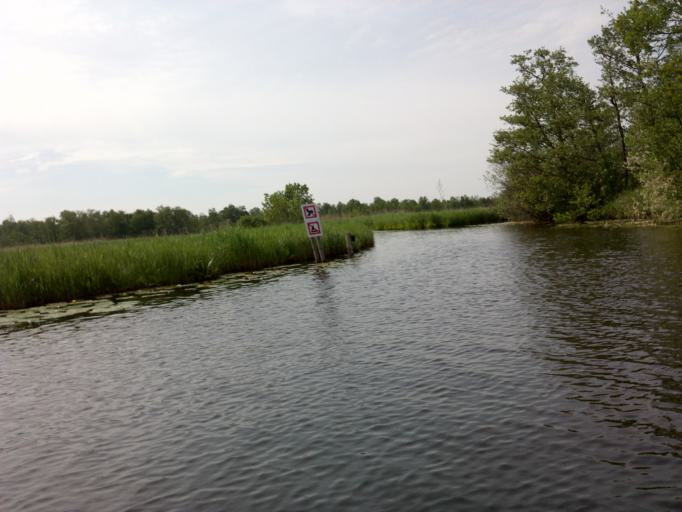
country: NL
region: South Holland
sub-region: Gemeente Nieuwkoop
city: Nieuwkoop
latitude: 52.1592
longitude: 4.8274
